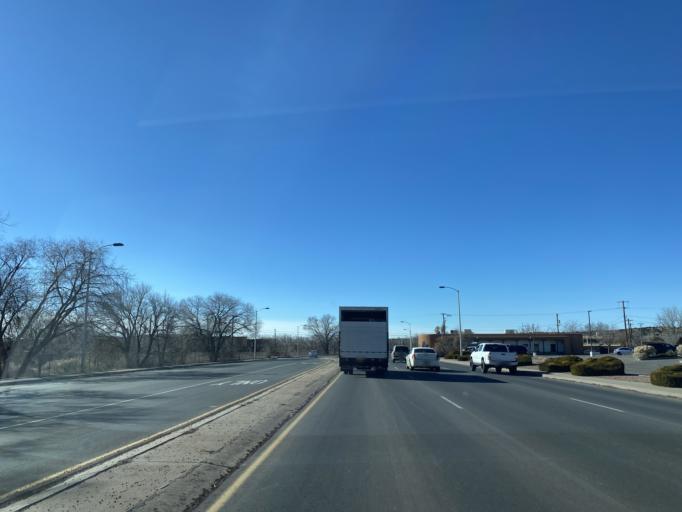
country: US
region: New Mexico
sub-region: Santa Fe County
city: Santa Fe
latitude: 35.6914
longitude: -105.9509
